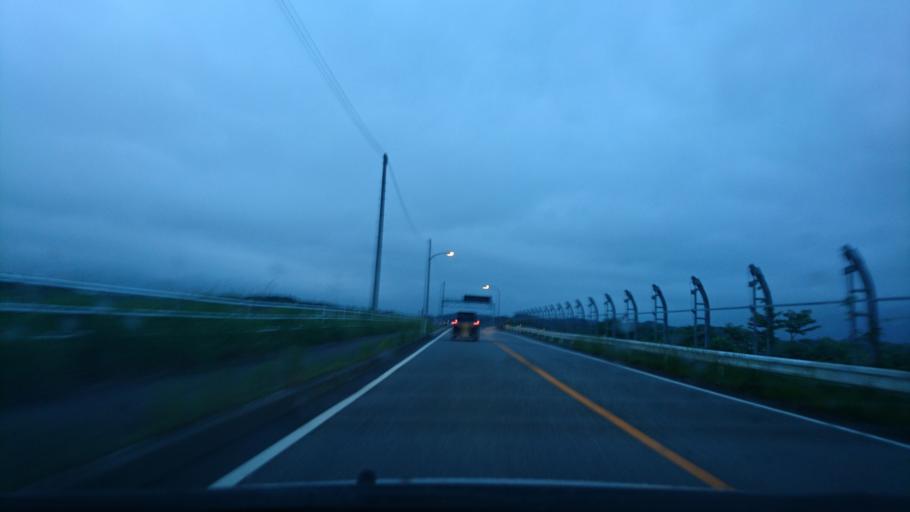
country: JP
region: Iwate
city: Ichinoseki
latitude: 38.8021
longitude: 141.0613
